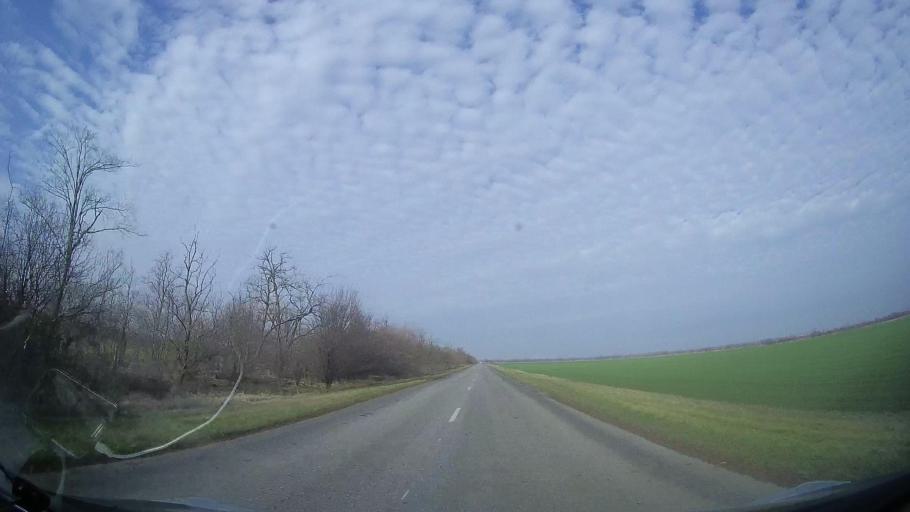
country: RU
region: Rostov
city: Gigant
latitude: 46.8655
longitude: 41.2773
